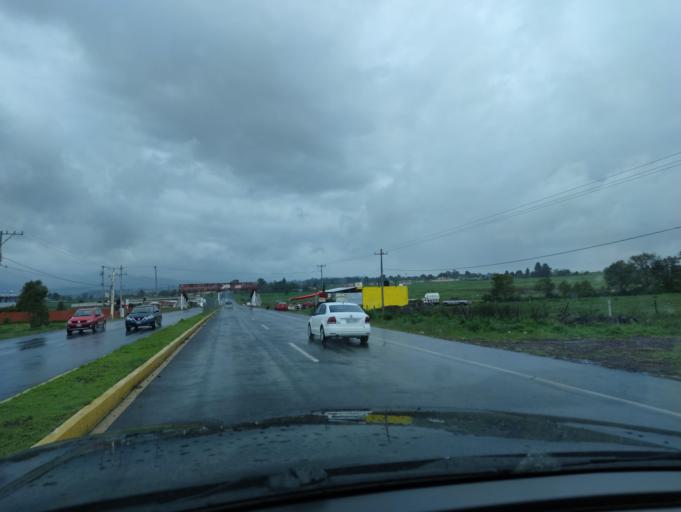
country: MX
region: Mexico
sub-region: Jilotepec
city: Doxhicho
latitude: 19.9219
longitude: -99.5896
